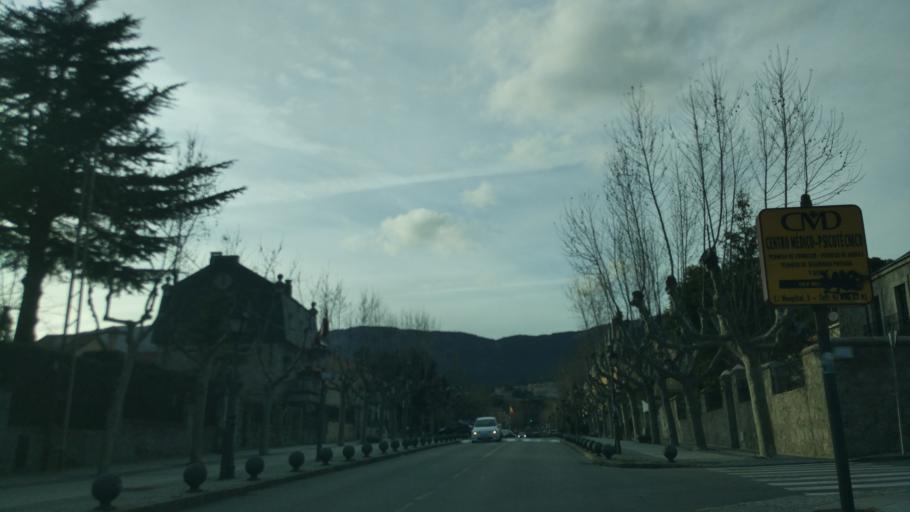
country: ES
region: Madrid
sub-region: Provincia de Madrid
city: El Escorial
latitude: 40.5818
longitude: -4.1279
